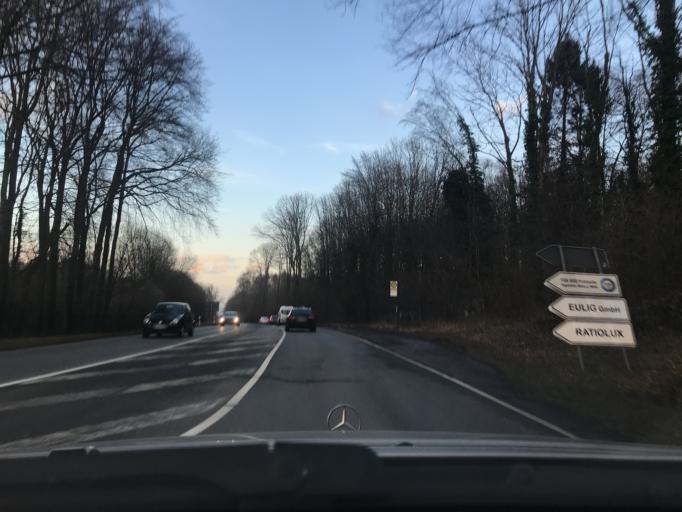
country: DE
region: North Rhine-Westphalia
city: Wickede
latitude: 51.5124
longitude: 7.8830
